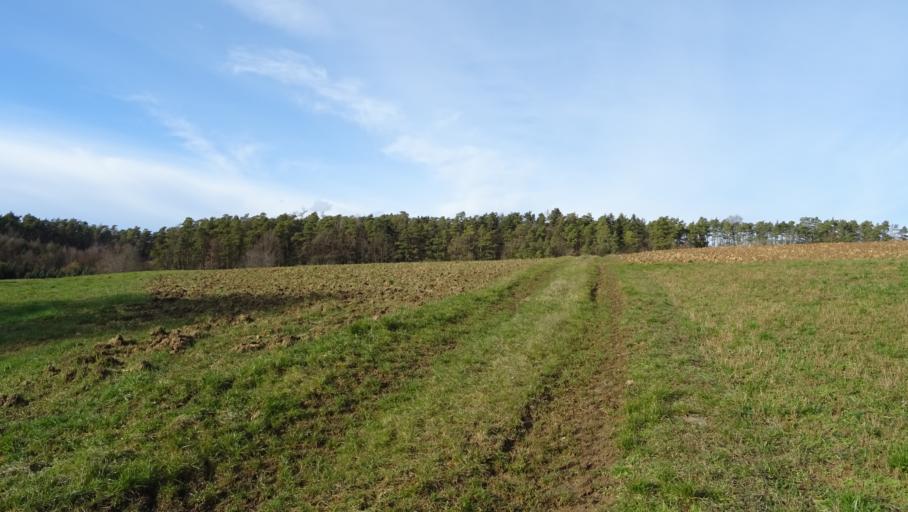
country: DE
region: Baden-Wuerttemberg
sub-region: Karlsruhe Region
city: Mosbach
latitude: 49.3668
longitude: 9.1918
